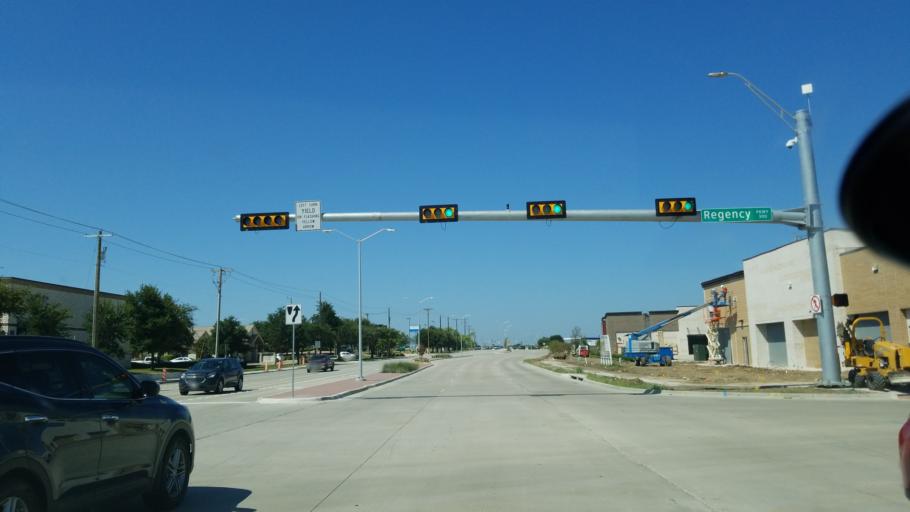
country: US
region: Texas
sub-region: Tarrant County
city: Mansfield
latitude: 32.5700
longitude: -97.1126
